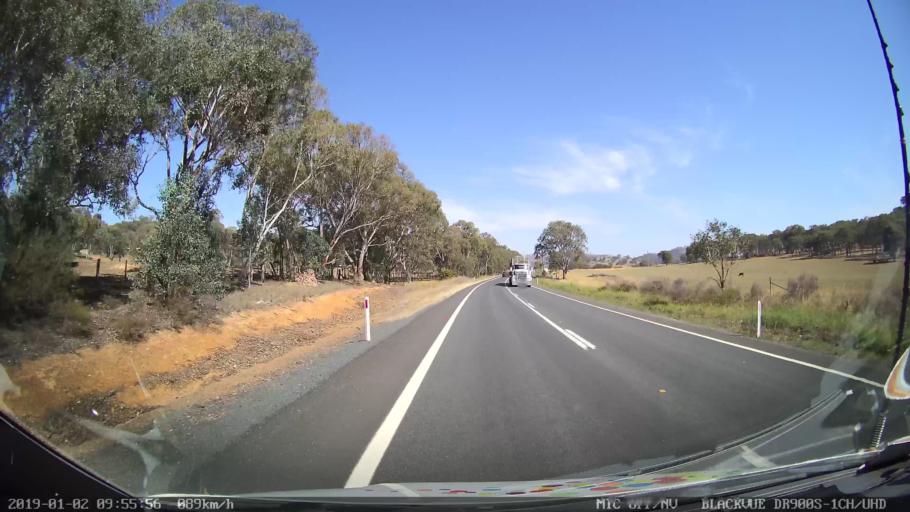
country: AU
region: New South Wales
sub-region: Tumut Shire
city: Tumut
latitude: -35.2197
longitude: 148.1820
